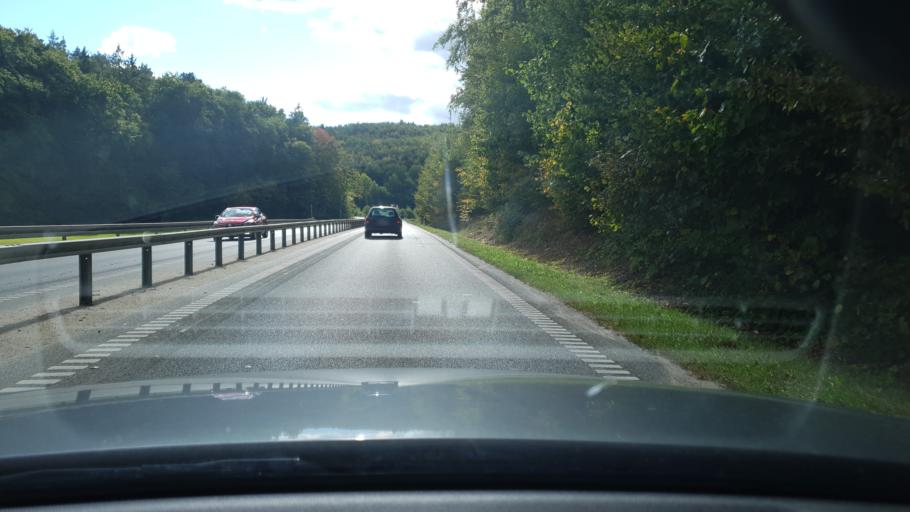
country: PL
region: Pomeranian Voivodeship
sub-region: Powiat wejherowski
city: Reda
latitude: 54.6242
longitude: 18.3402
